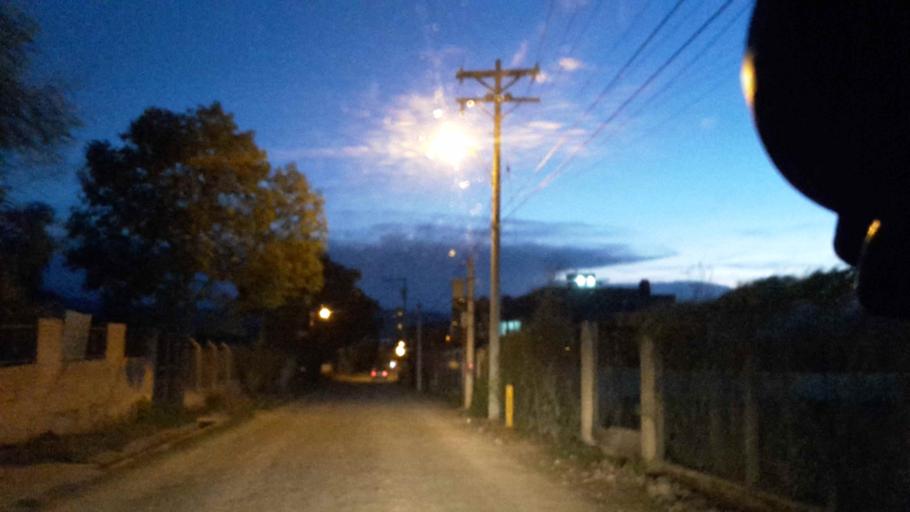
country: BO
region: Cochabamba
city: Cochabamba
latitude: -17.3332
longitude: -66.2183
